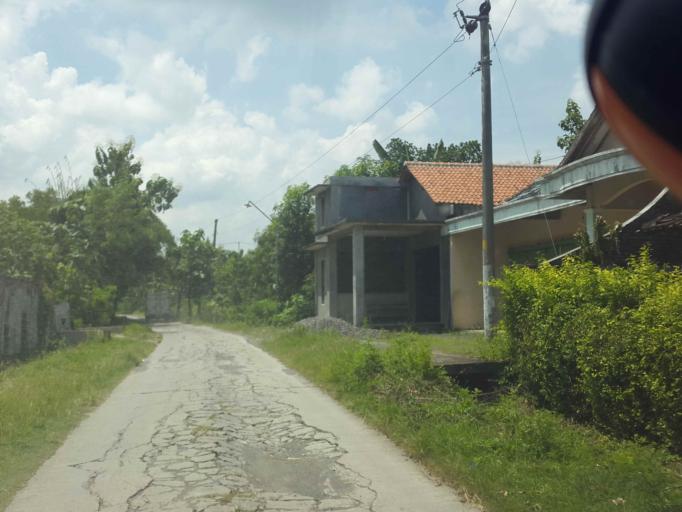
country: ID
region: Central Java
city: Sragen
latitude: -7.3119
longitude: 110.8796
